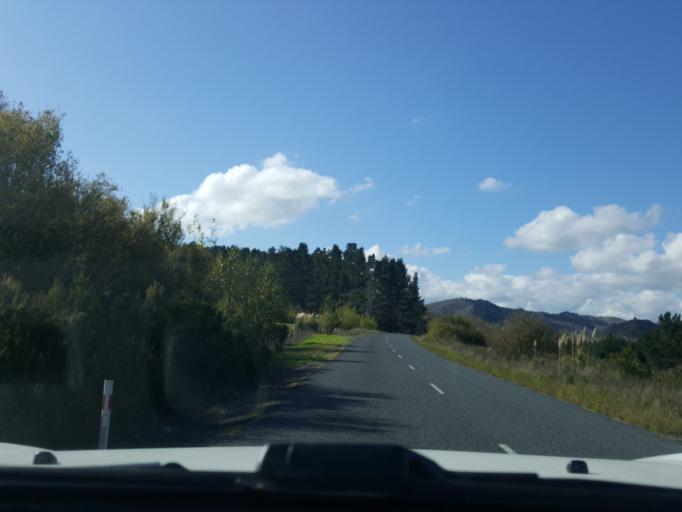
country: NZ
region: Waikato
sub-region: Waikato District
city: Ngaruawahia
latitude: -37.5332
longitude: 175.1794
